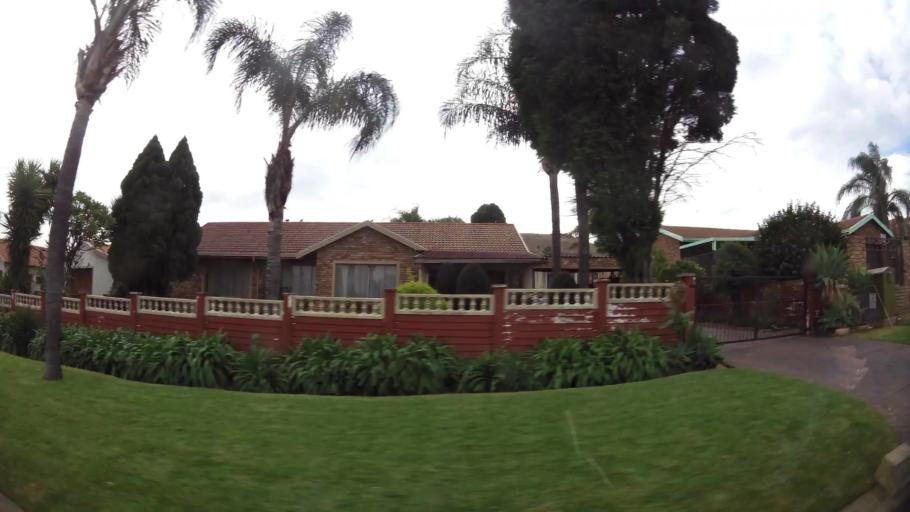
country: ZA
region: Gauteng
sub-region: City of Tshwane Metropolitan Municipality
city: Pretoria
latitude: -25.6995
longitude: 28.3021
